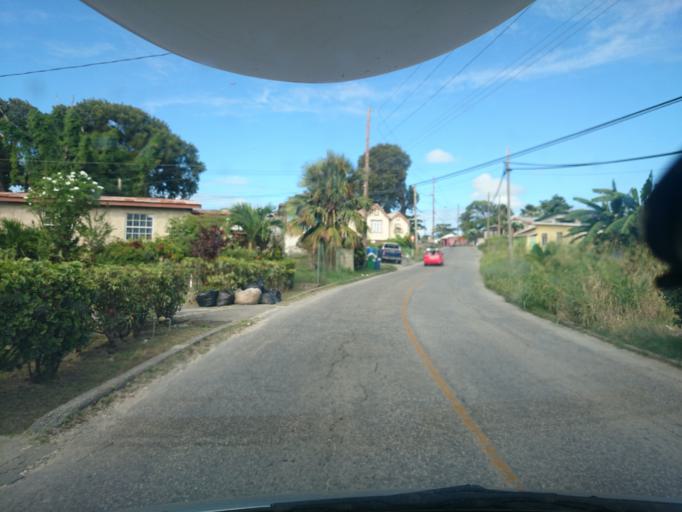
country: BB
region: Christ Church
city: Oistins
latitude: 13.0690
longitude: -59.5413
